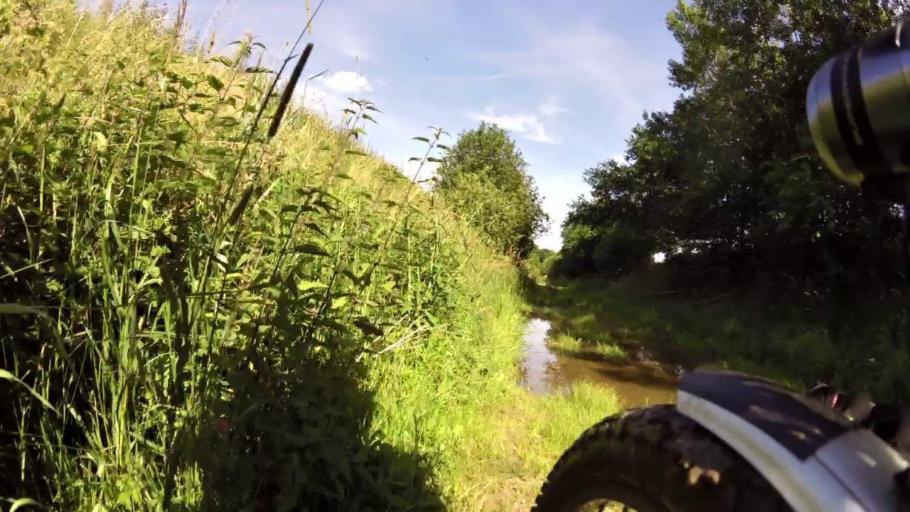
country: PL
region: West Pomeranian Voivodeship
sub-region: Powiat lobeski
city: Radowo Male
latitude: 53.5865
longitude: 15.4178
